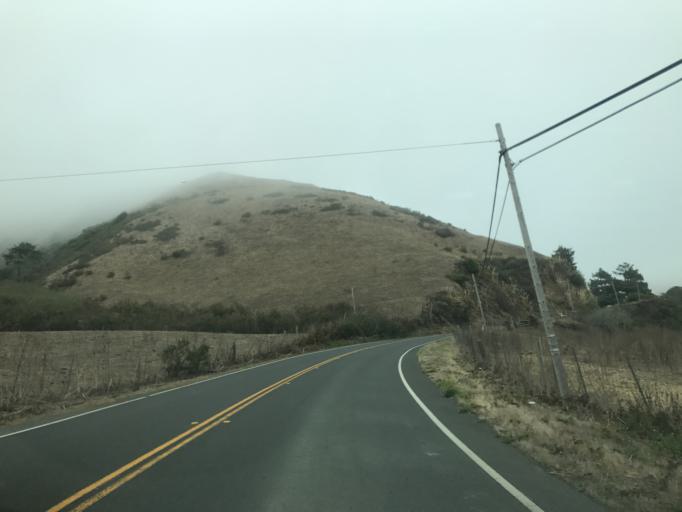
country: US
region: California
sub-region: Sonoma County
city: Monte Rio
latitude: 38.4427
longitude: -123.1007
